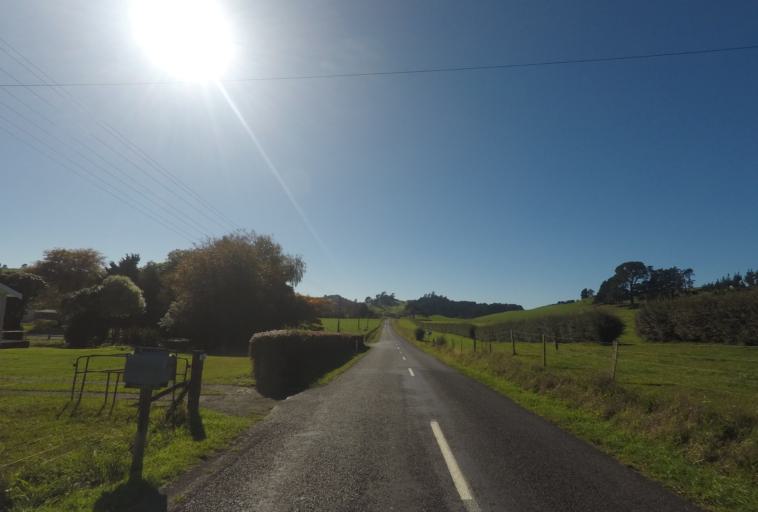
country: NZ
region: Bay of Plenty
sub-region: Western Bay of Plenty District
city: Waihi Beach
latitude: -37.4101
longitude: 175.8950
